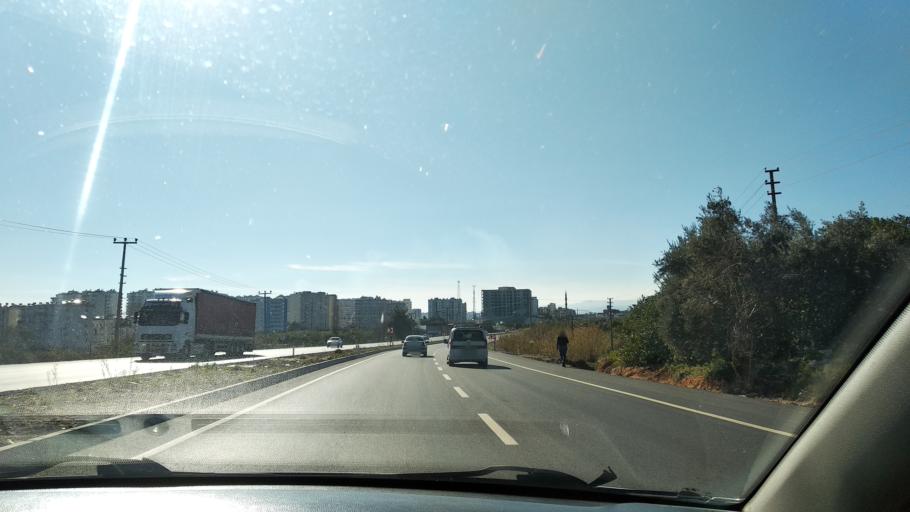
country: TR
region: Mersin
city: Tomuk
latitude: 36.6559
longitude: 34.3908
